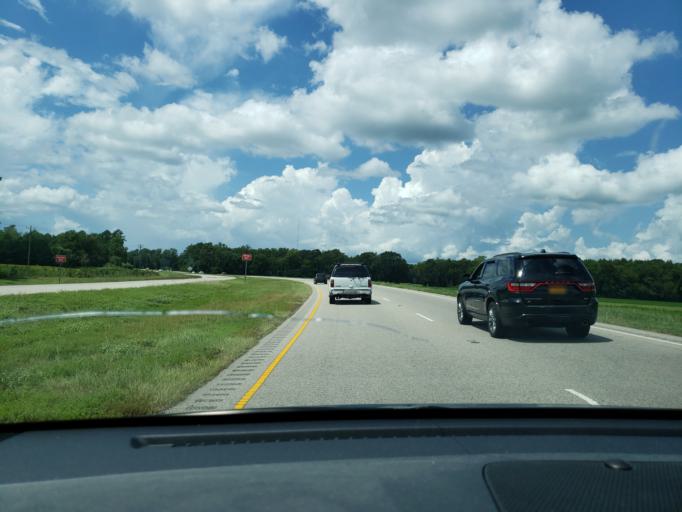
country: US
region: North Carolina
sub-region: Bladen County
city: Elizabethtown
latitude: 34.7217
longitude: -78.7582
